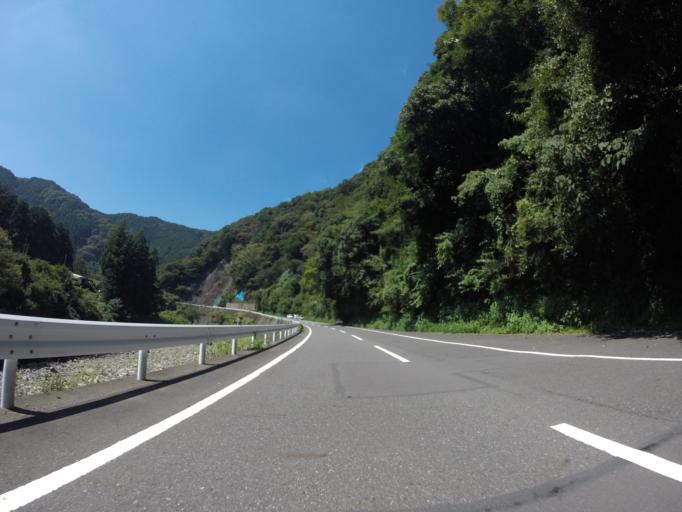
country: JP
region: Shizuoka
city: Shizuoka-shi
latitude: 35.0496
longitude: 138.2455
